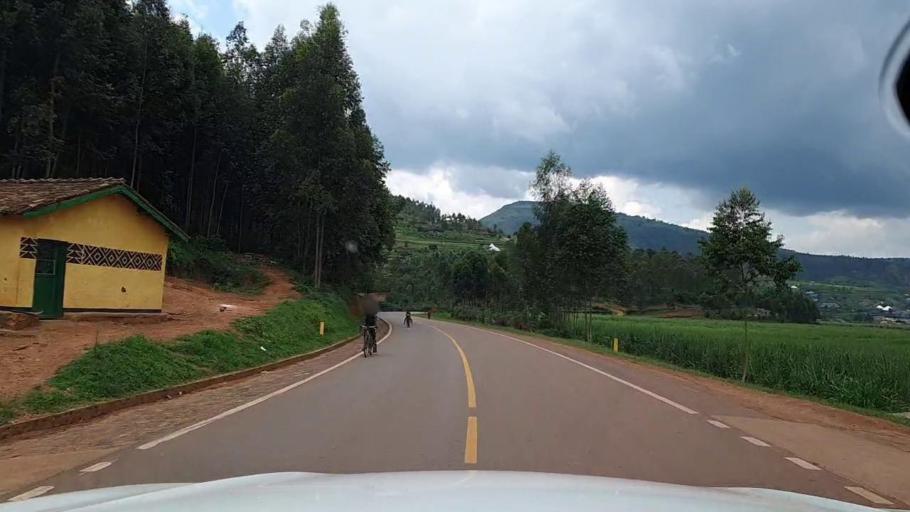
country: RW
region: Kigali
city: Kigali
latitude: -1.7785
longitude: 30.1295
